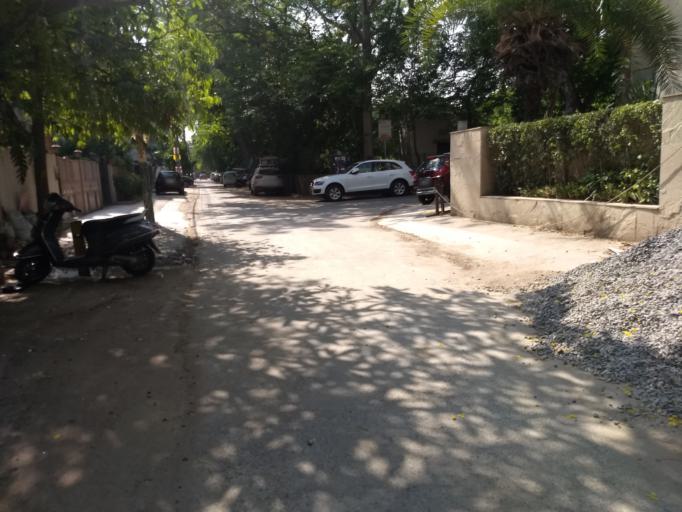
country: IN
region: NCT
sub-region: New Delhi
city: New Delhi
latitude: 28.5659
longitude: 77.1968
